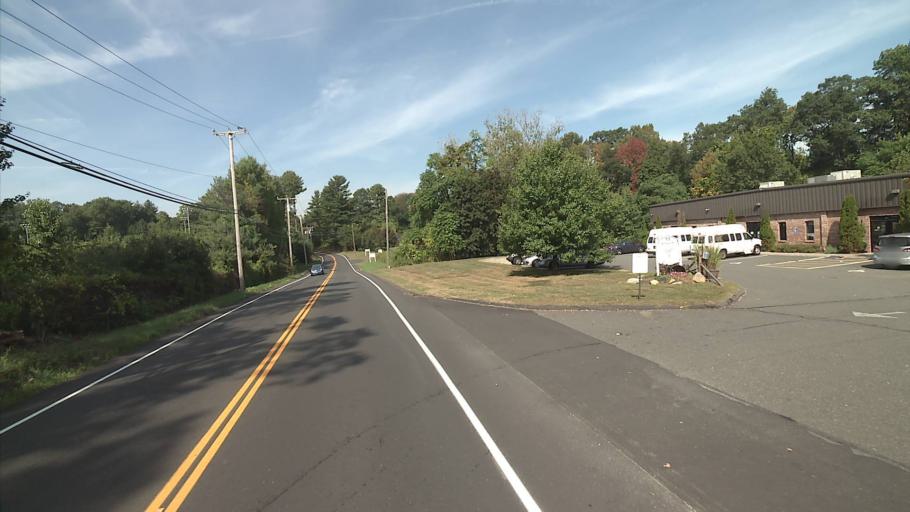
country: US
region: Connecticut
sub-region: Fairfield County
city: Newtown
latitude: 41.4123
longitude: -73.2714
